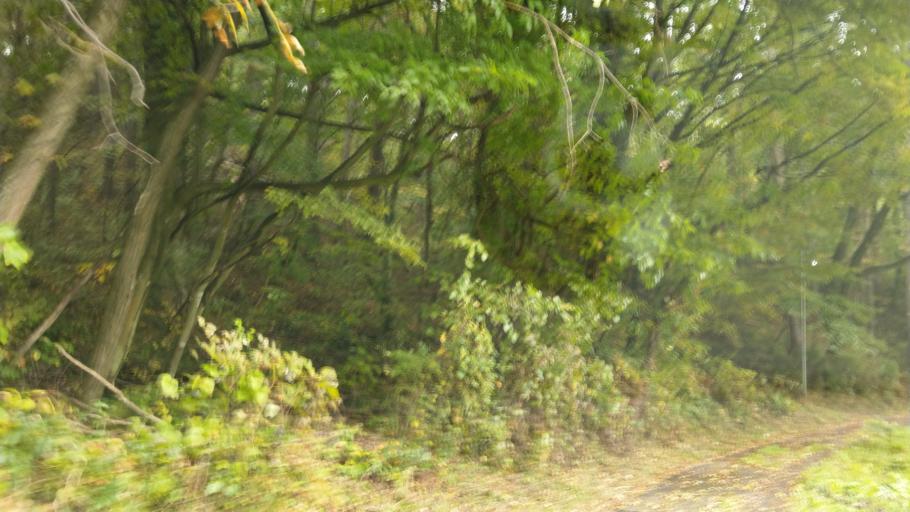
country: JP
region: Nagano
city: Komoro
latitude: 36.3558
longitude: 138.4186
